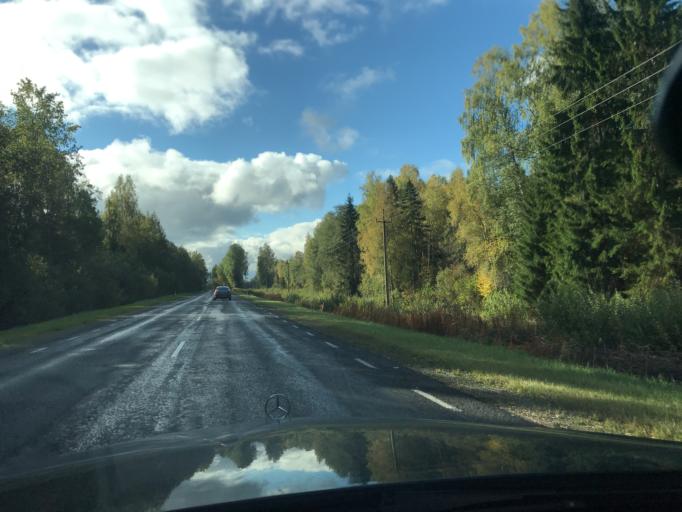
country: EE
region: Tartu
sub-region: Elva linn
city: Elva
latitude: 57.9955
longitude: 26.2661
